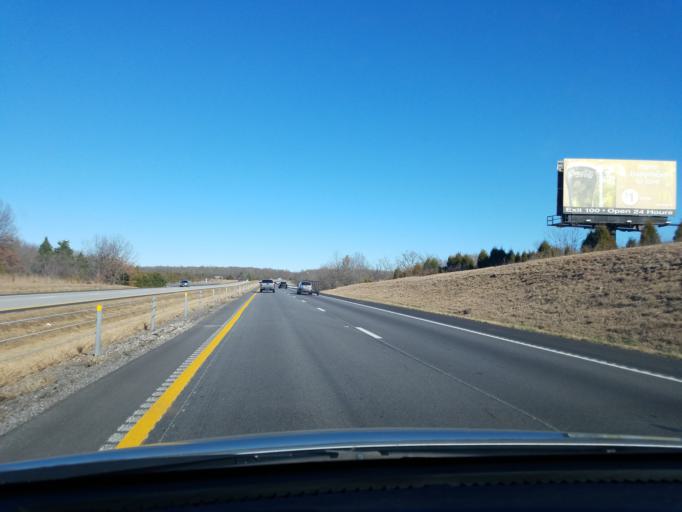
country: US
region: Missouri
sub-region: Webster County
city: Marshfield
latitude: 37.3203
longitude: -92.9618
